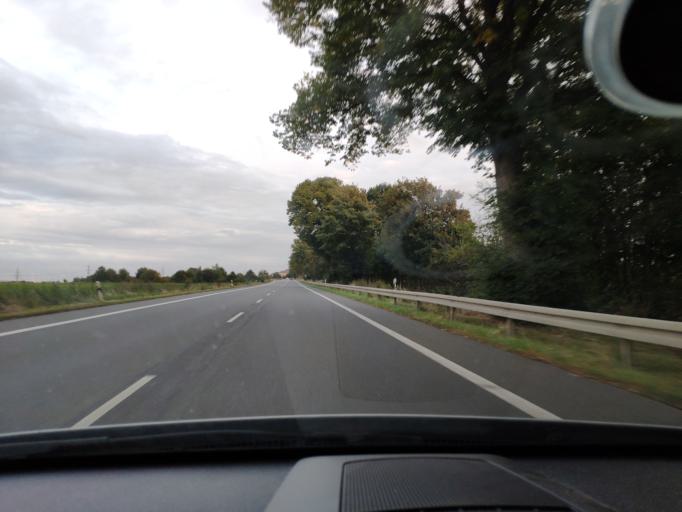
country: DE
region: North Rhine-Westphalia
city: Baesweiler
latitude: 50.9445
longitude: 6.1900
